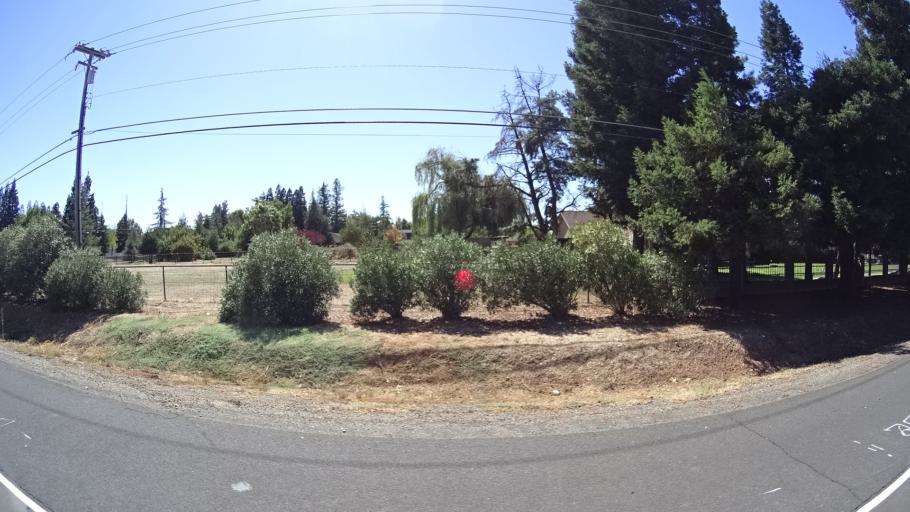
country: US
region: California
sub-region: Sacramento County
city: Vineyard
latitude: 38.4381
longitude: -121.3618
